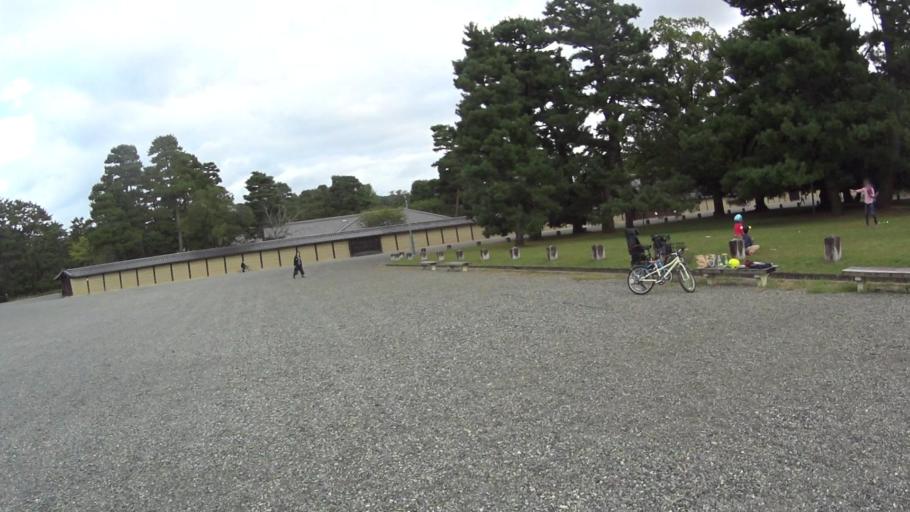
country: JP
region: Kyoto
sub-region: Kyoto-shi
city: Kamigyo-ku
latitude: 35.0230
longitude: 135.7634
